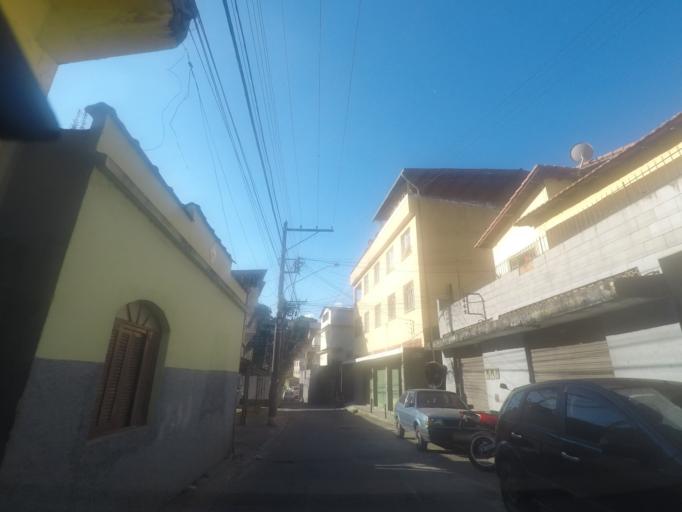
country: BR
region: Rio de Janeiro
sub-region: Petropolis
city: Petropolis
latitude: -22.4975
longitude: -43.1486
